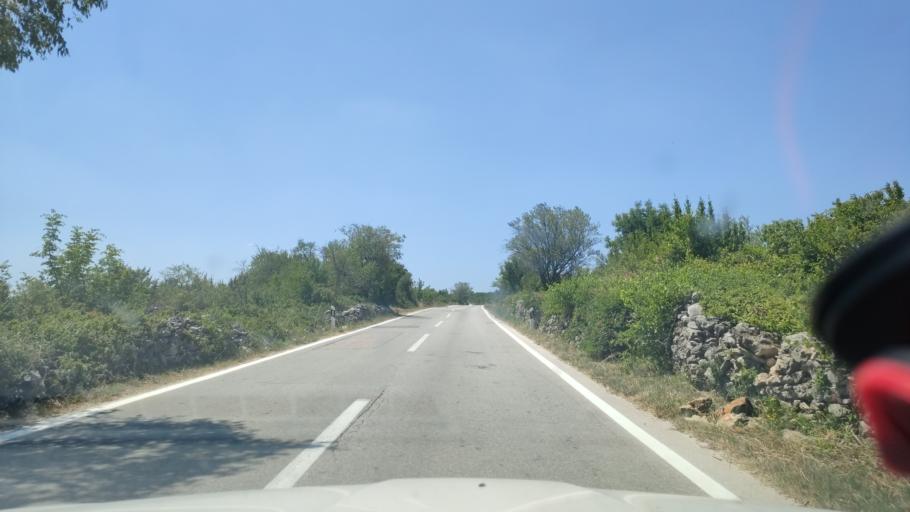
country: HR
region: Sibensko-Kniniska
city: Kistanje
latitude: 44.0094
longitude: 16.0055
